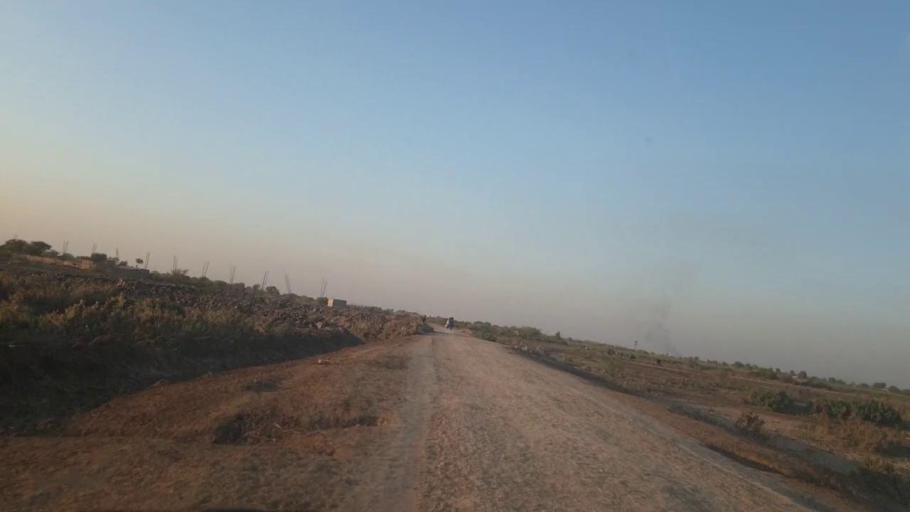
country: PK
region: Sindh
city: Mirpur Khas
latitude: 25.4621
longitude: 69.0718
